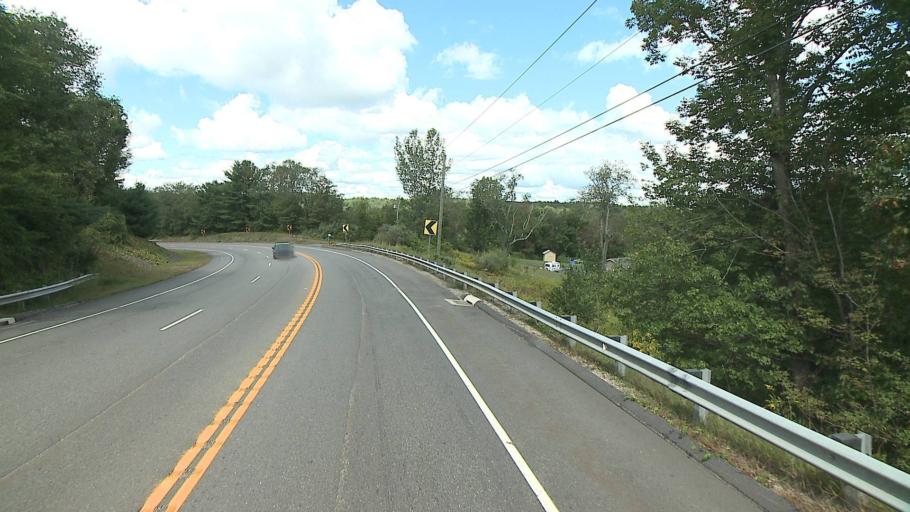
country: US
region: Connecticut
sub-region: Windham County
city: South Woodstock
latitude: 41.8784
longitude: -72.0796
